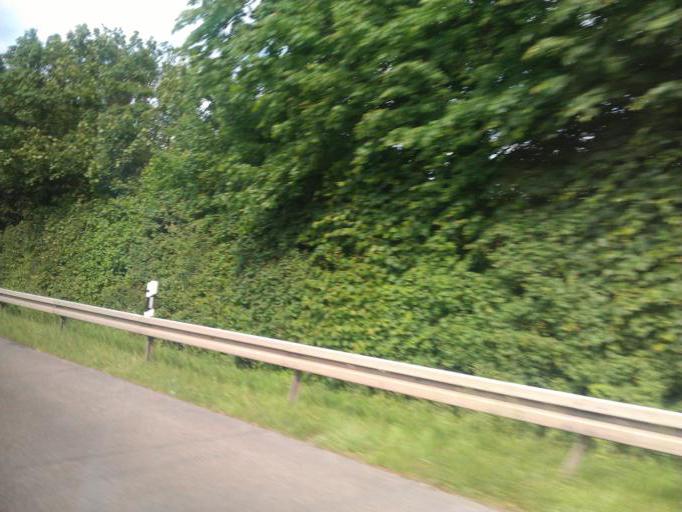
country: DE
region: North Rhine-Westphalia
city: Wesseling
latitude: 50.8377
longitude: 6.9664
